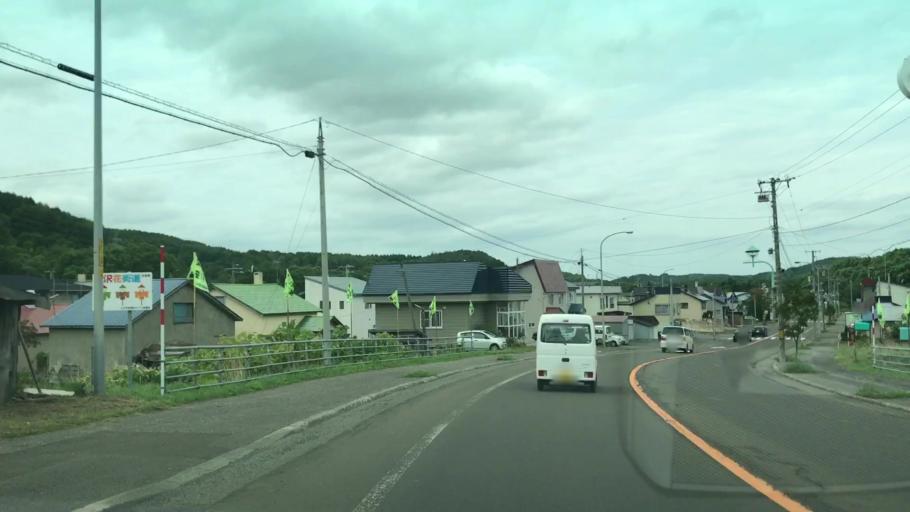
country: JP
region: Hokkaido
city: Iwanai
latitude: 42.9695
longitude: 140.6790
